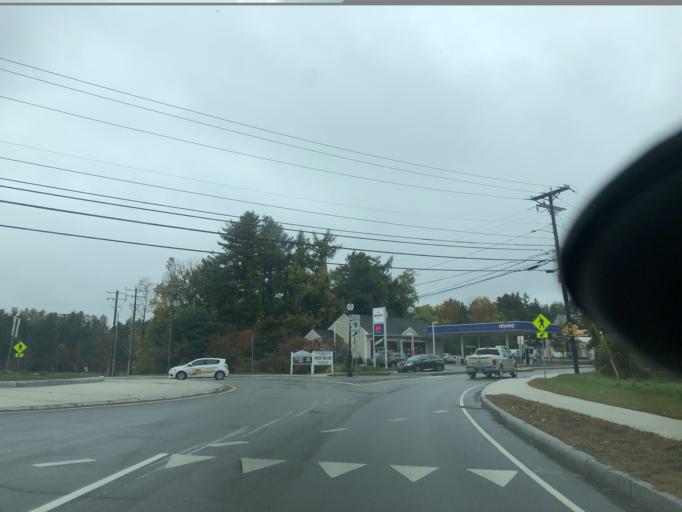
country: US
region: New Hampshire
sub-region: Strafford County
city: Dover
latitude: 43.1883
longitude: -70.8863
